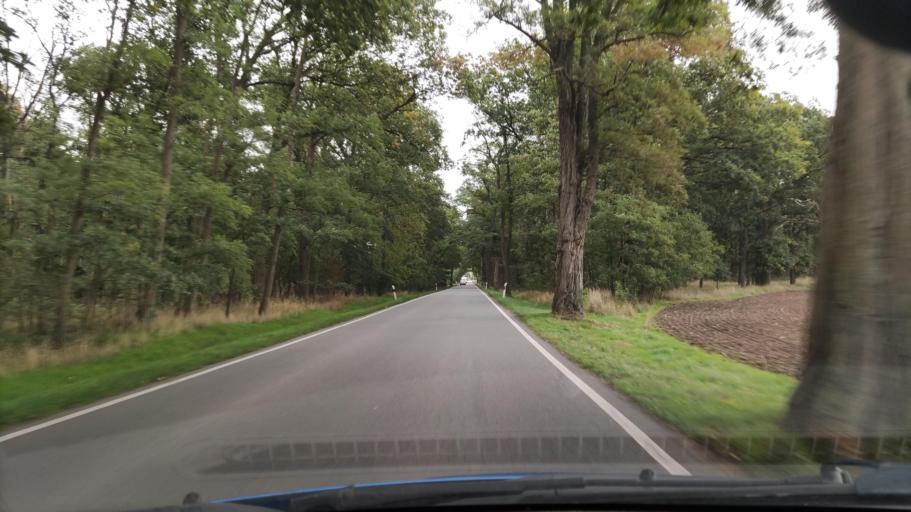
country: DE
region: Saxony-Anhalt
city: Pretzier
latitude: 52.8217
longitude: 11.3712
